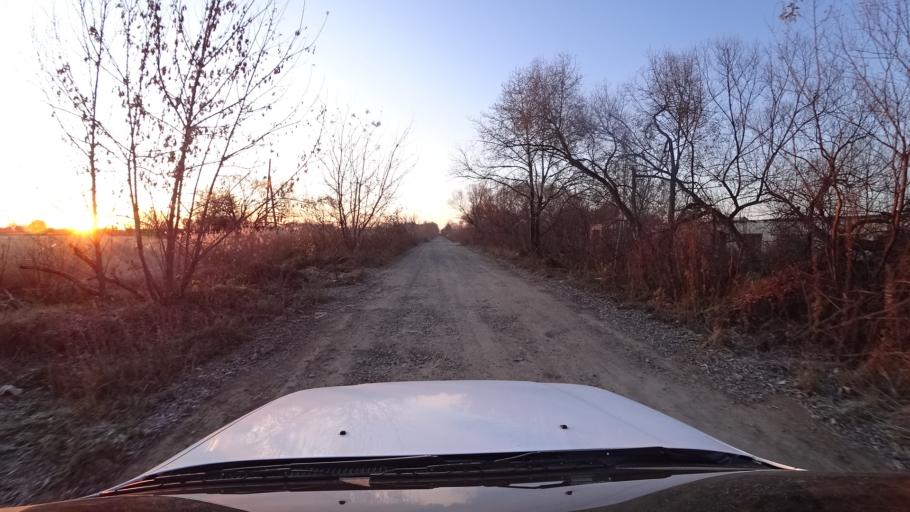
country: RU
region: Primorskiy
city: Dal'nerechensk
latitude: 45.9197
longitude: 133.7371
